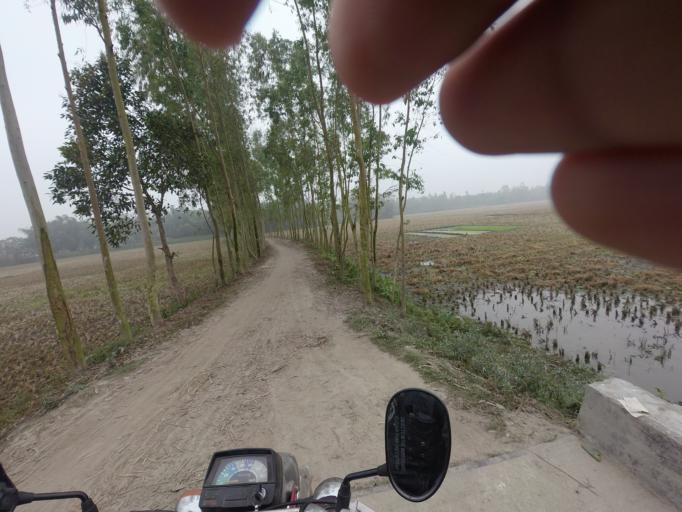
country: BD
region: Rajshahi
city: Saidpur
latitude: 26.0376
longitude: 88.8650
